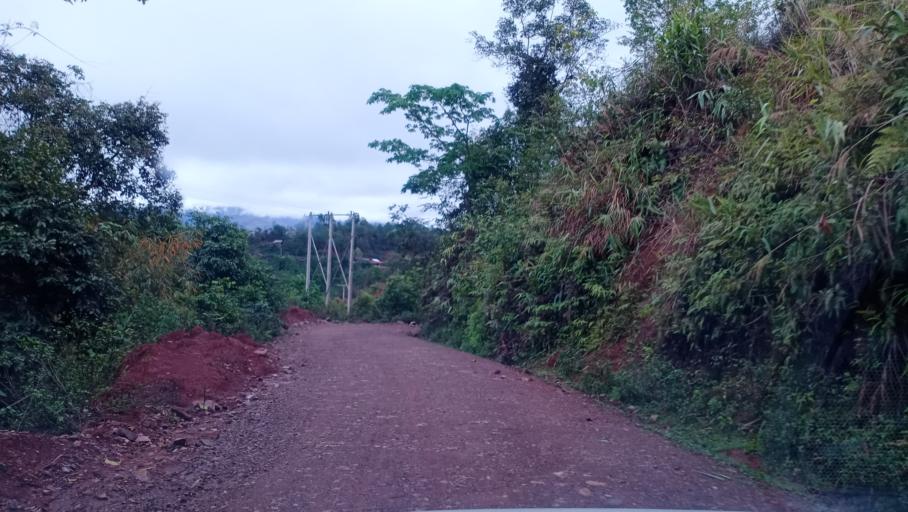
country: LA
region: Phongsali
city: Phongsali
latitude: 21.3392
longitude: 102.0770
